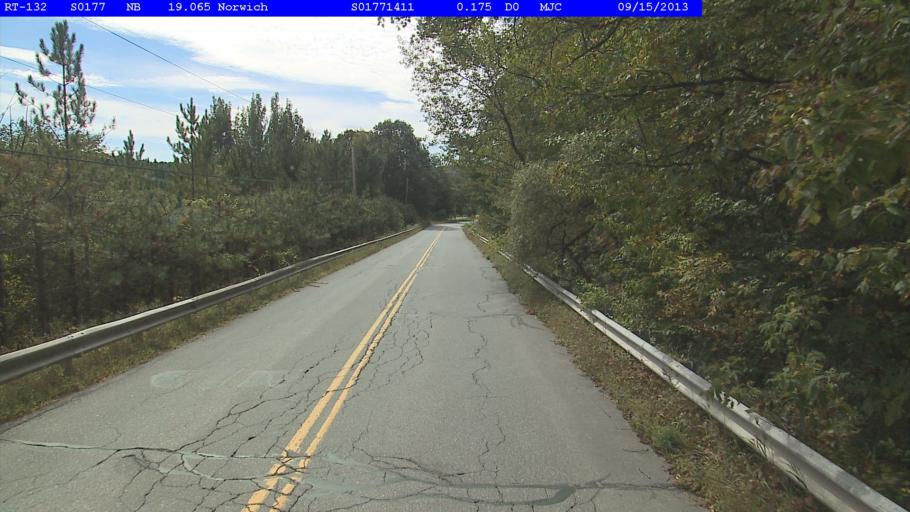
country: US
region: New Hampshire
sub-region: Grafton County
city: Hanover
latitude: 43.7842
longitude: -72.2581
